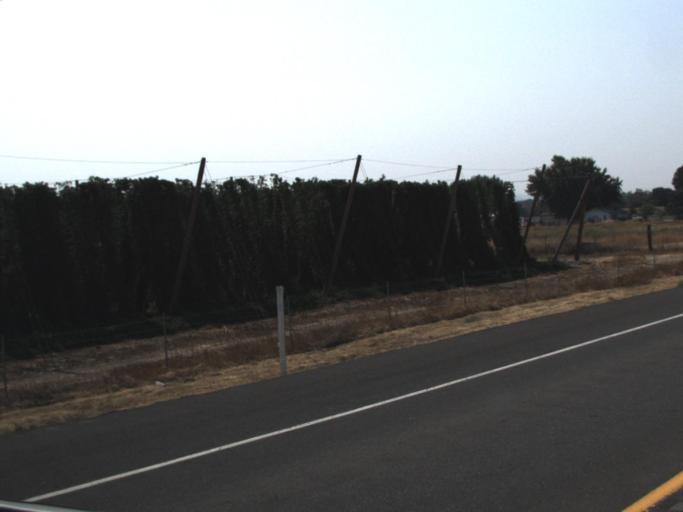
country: US
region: Washington
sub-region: Yakima County
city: Terrace Heights
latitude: 46.5770
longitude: -120.4451
